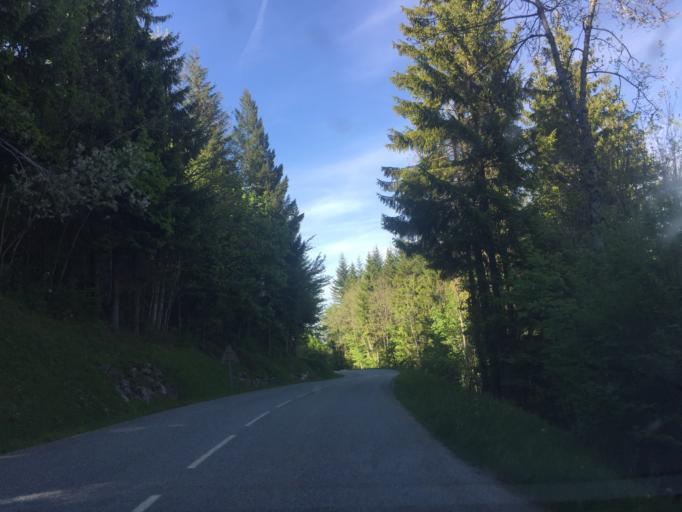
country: FR
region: Rhone-Alpes
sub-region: Departement de la Savoie
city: Saint-Baldoph
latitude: 45.4815
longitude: 5.9151
